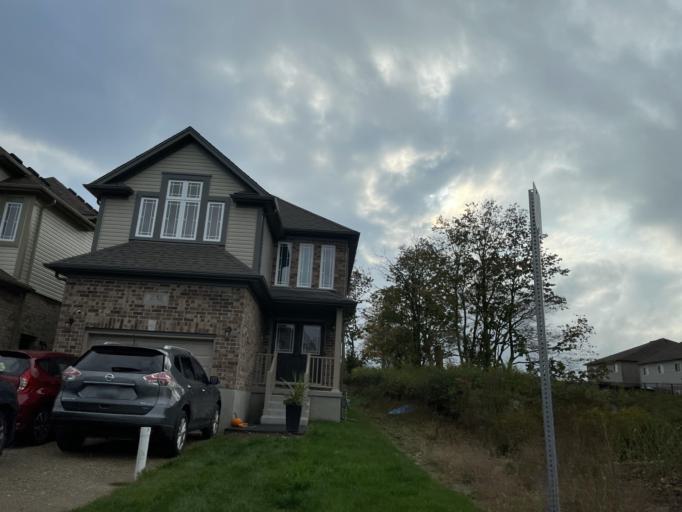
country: CA
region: Ontario
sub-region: Wellington County
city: Guelph
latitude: 43.5277
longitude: -80.1982
